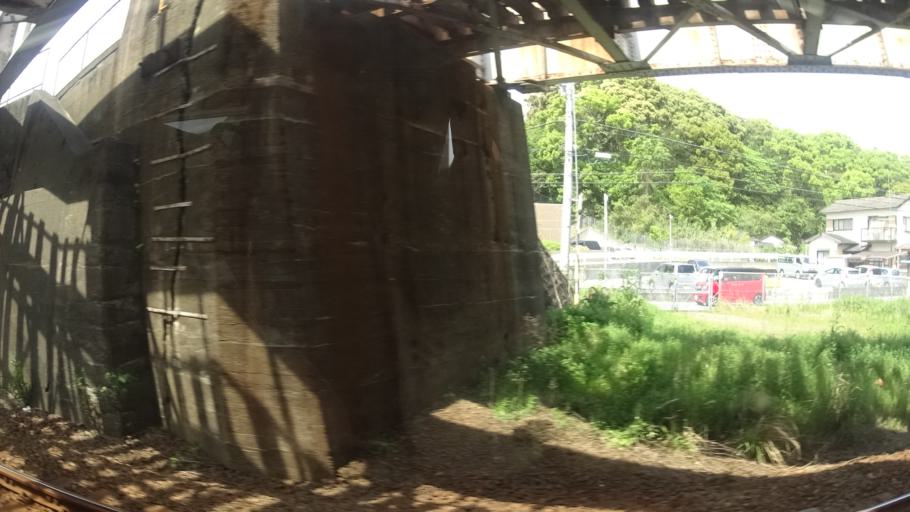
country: JP
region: Mie
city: Tsu-shi
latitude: 34.7377
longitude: 136.5106
